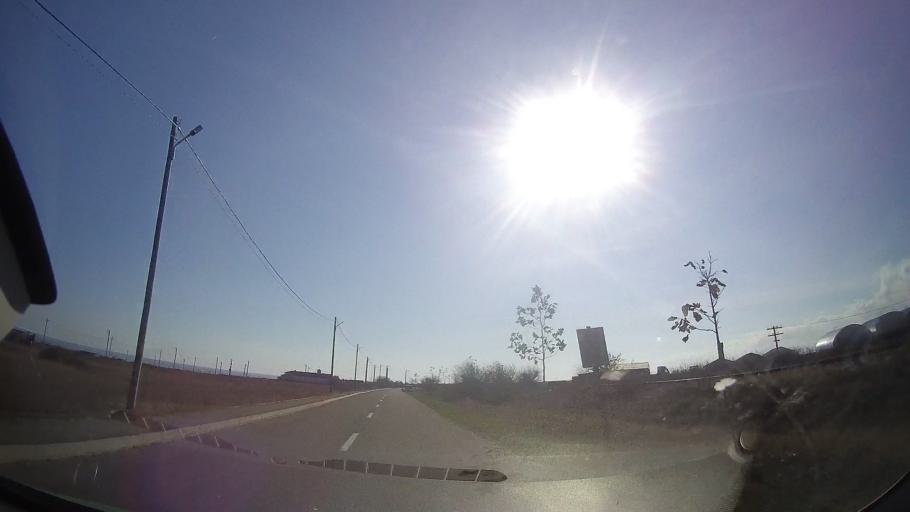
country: RO
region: Constanta
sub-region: Comuna Costinesti
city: Schitu
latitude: 43.9275
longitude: 28.6323
